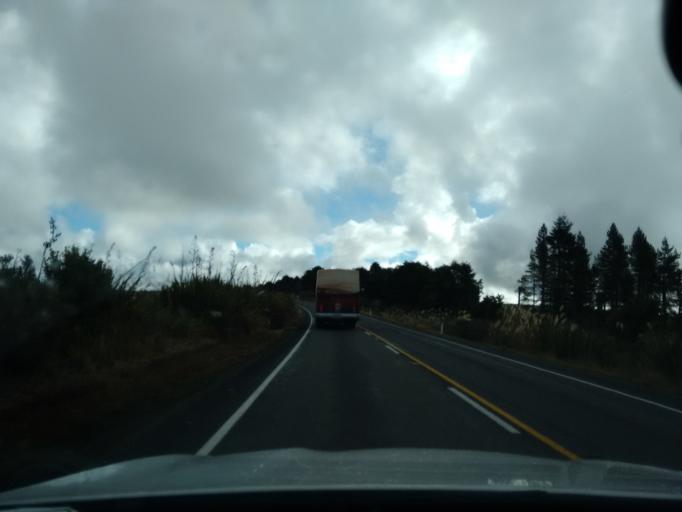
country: NZ
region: Manawatu-Wanganui
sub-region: Ruapehu District
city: Waiouru
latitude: -39.1800
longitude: 175.4498
